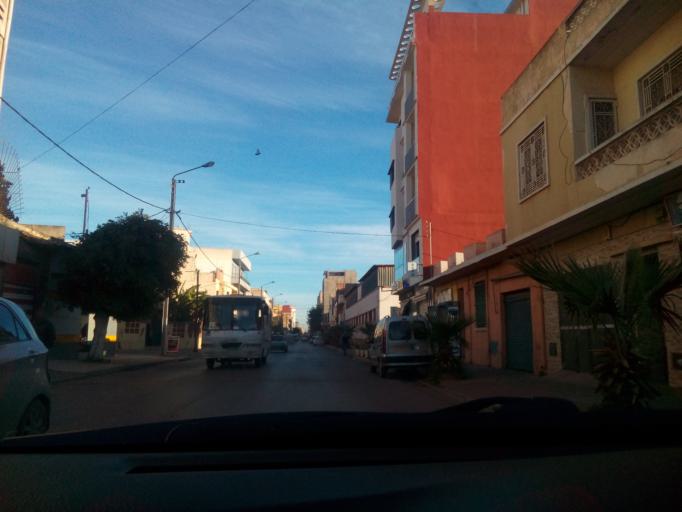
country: DZ
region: Oran
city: Oran
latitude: 35.6823
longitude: -0.6587
